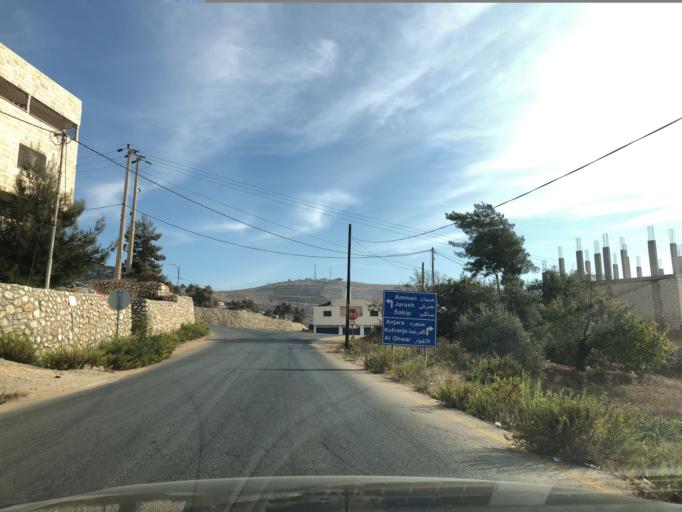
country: JO
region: Irbid
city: `Anjarah
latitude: 32.3155
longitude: 35.7712
